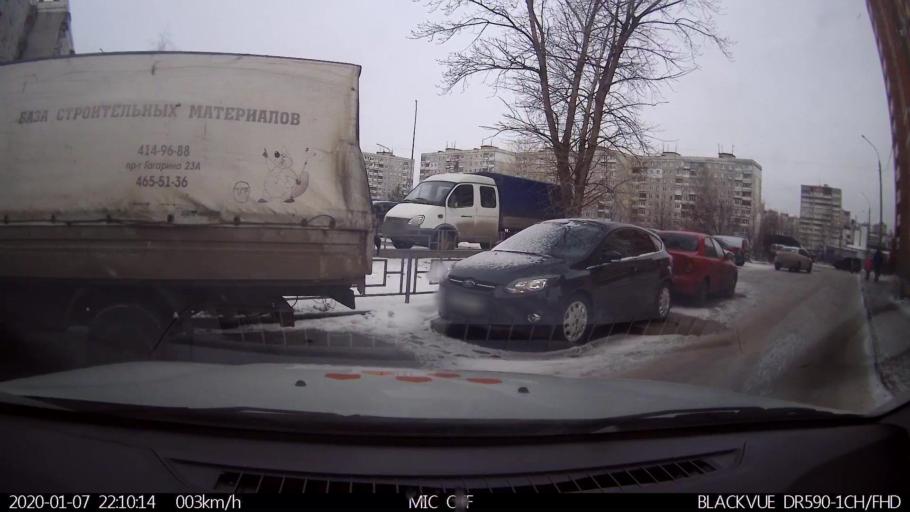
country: RU
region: Nizjnij Novgorod
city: Nizhniy Novgorod
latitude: 56.3428
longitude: 43.9254
